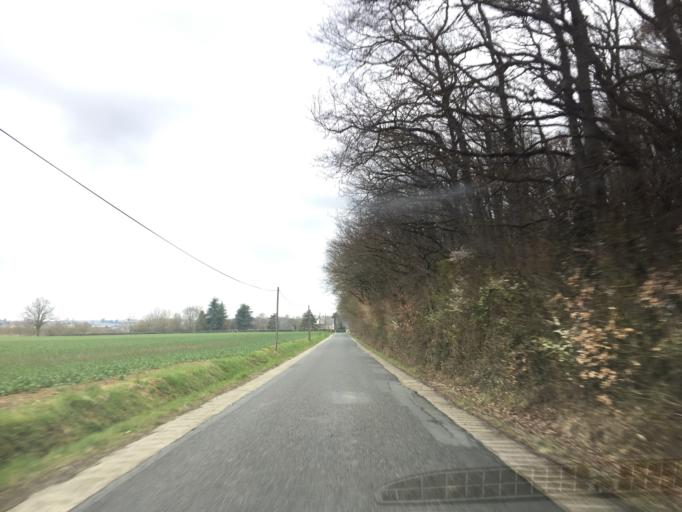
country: FR
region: Centre
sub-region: Departement d'Indre-et-Loire
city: Chanceaux-sur-Choisille
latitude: 47.4721
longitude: 0.7295
